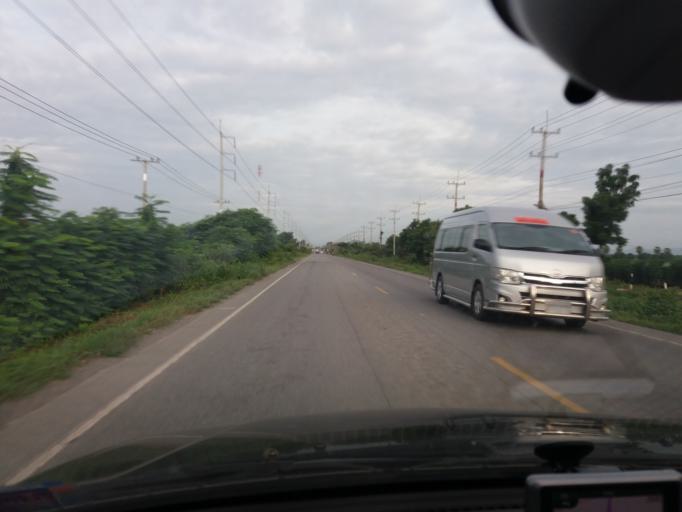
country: TH
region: Suphan Buri
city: U Thong
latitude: 14.3356
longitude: 99.7973
